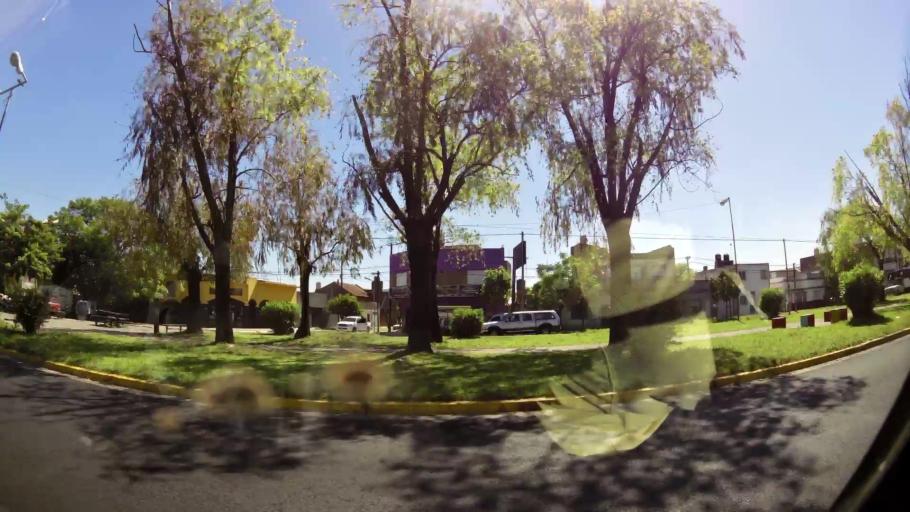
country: AR
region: Buenos Aires
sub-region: Partido de Quilmes
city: Quilmes
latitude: -34.7128
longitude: -58.3040
